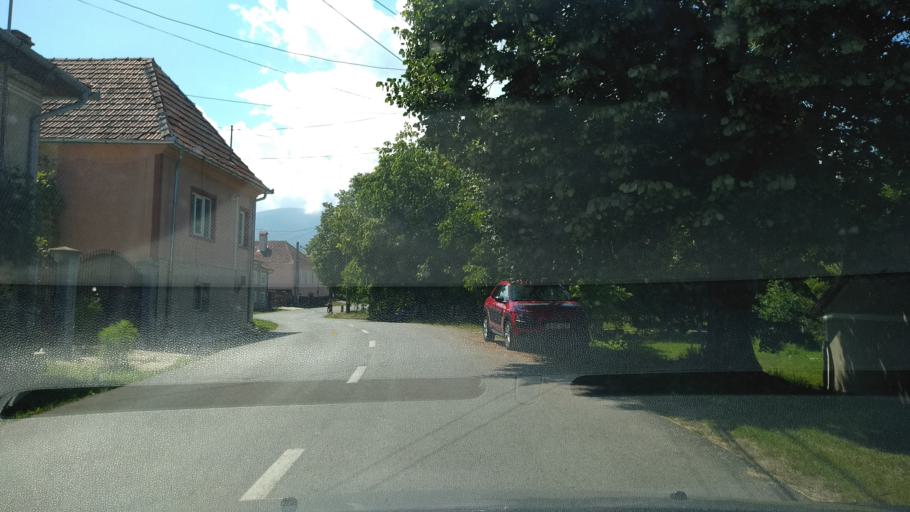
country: RO
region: Hunedoara
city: Salasu de Sus
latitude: 45.5118
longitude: 22.9554
